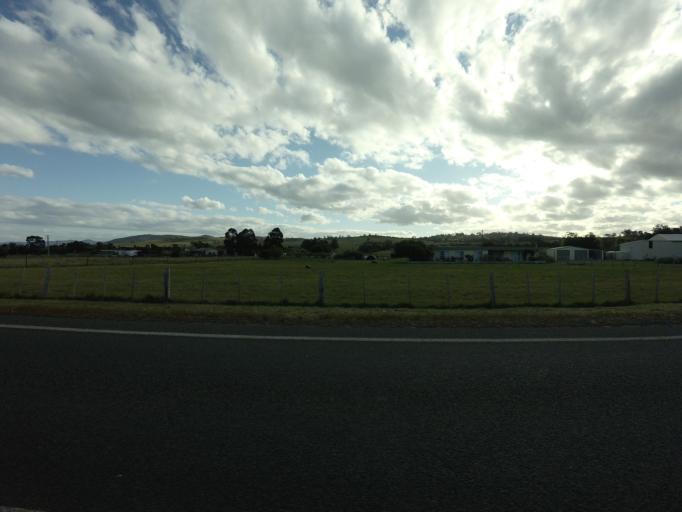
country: AU
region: Tasmania
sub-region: Sorell
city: Sorell
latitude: -42.7371
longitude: 147.5307
